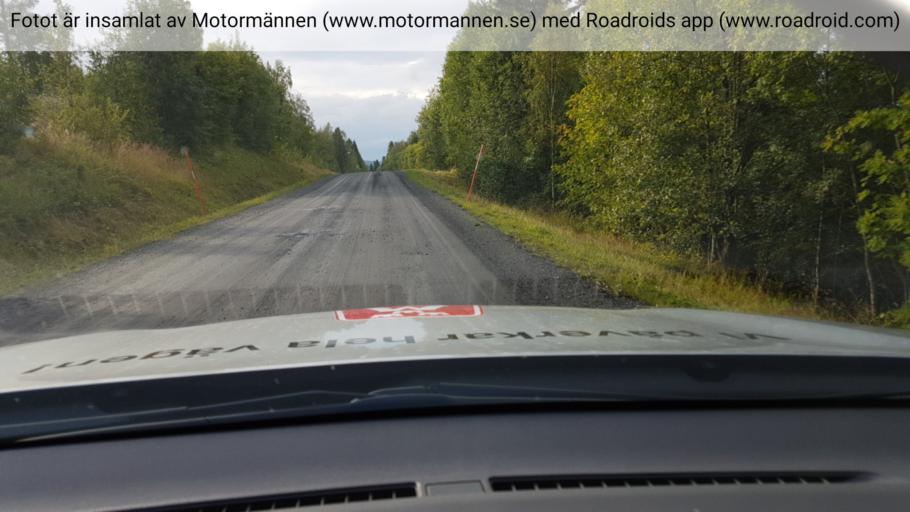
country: SE
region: Jaemtland
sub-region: Stroemsunds Kommun
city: Stroemsund
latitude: 64.1427
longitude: 15.7151
